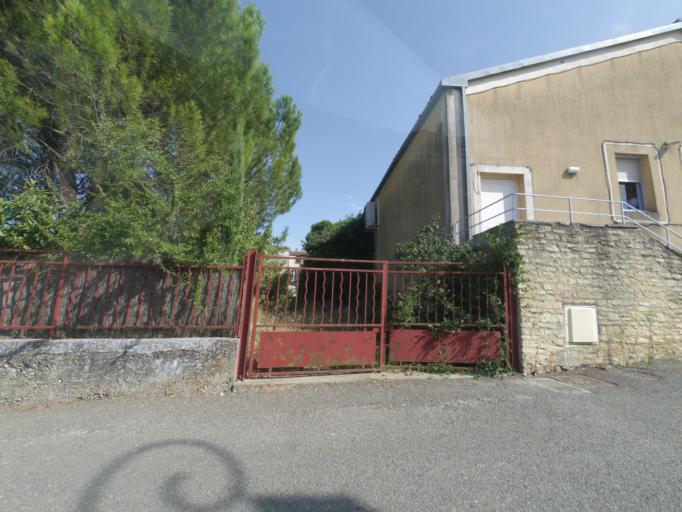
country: FR
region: Languedoc-Roussillon
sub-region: Departement du Gard
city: Saint-Mamert-du-Gard
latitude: 43.9090
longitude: 4.1938
